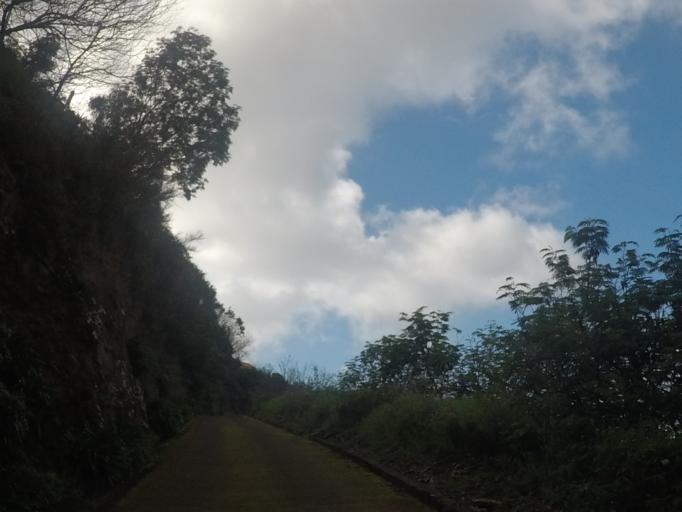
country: PT
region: Madeira
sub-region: Calheta
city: Faja da Ovelha
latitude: 32.8141
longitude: -17.2433
